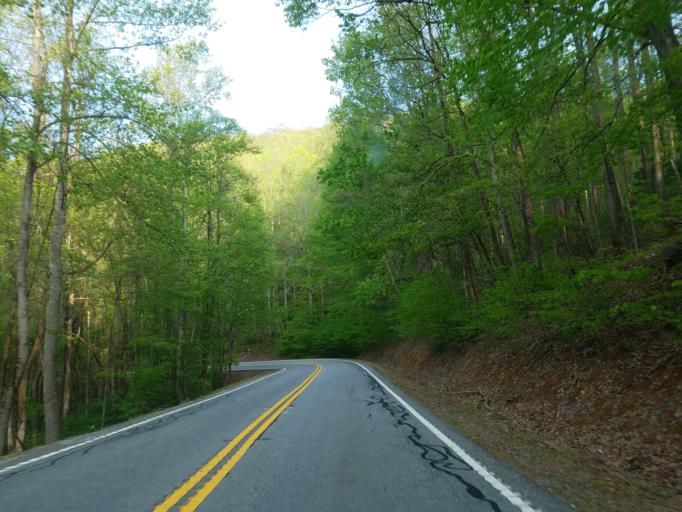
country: US
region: Georgia
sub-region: Fannin County
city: Blue Ridge
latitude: 34.8115
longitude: -84.1860
